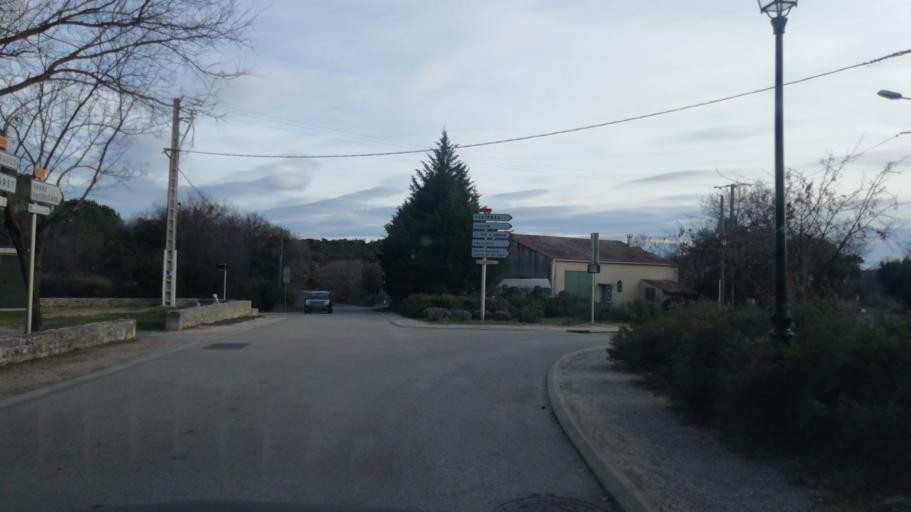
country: FR
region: Languedoc-Roussillon
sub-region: Departement de l'Herault
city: Claret
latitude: 43.8371
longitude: 3.9205
